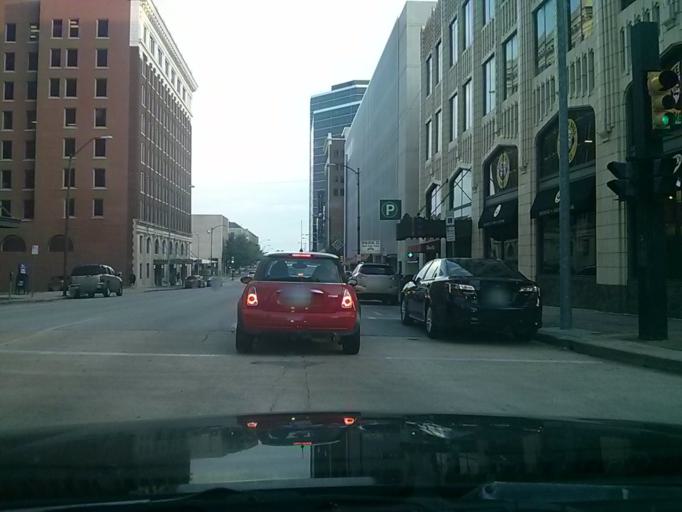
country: US
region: Oklahoma
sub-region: Tulsa County
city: Tulsa
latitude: 36.1511
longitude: -95.9912
